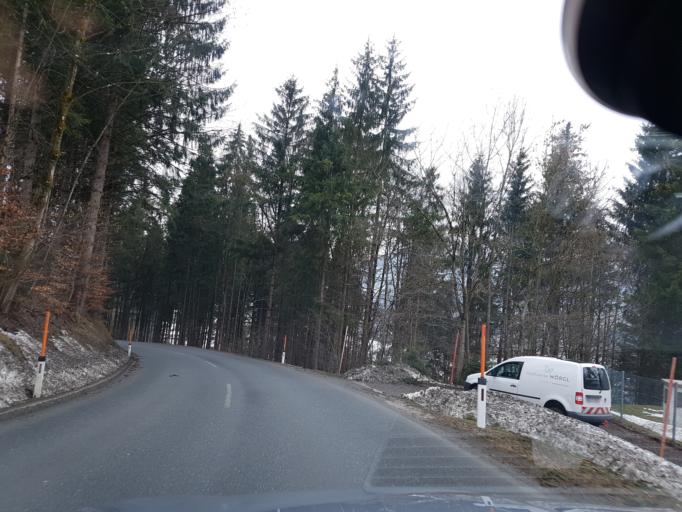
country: AT
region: Tyrol
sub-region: Politischer Bezirk Kufstein
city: Worgl
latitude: 47.4790
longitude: 12.0717
